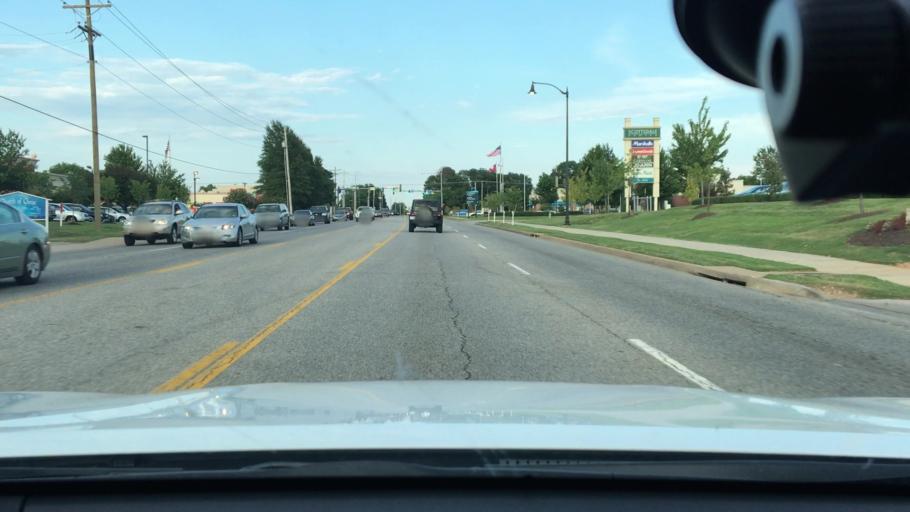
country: US
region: Arkansas
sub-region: Benton County
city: Bentonville
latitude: 36.3348
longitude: -94.1773
